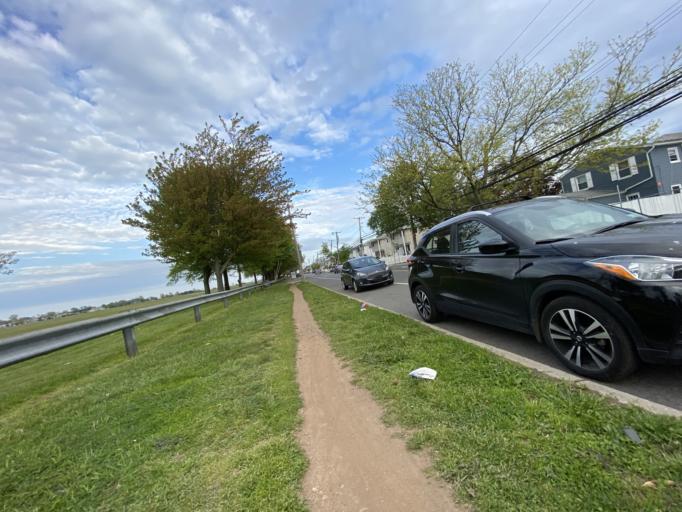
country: US
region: New York
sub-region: Richmond County
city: Staten Island
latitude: 40.5685
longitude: -74.1058
